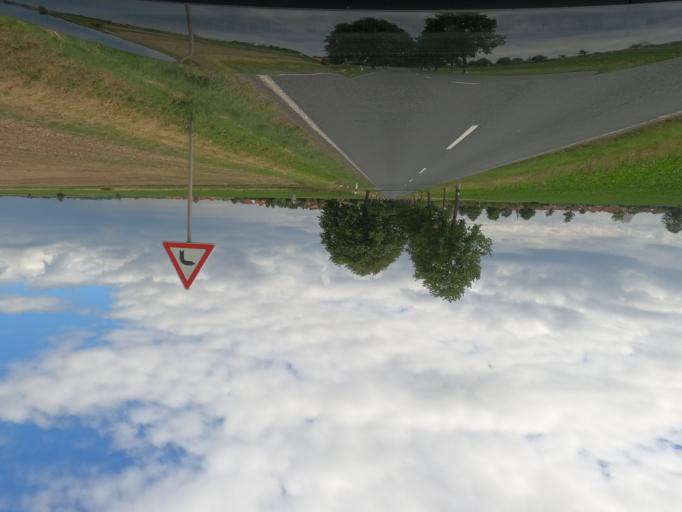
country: DE
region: Lower Saxony
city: Algermissen
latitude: 52.2499
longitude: 9.9883
